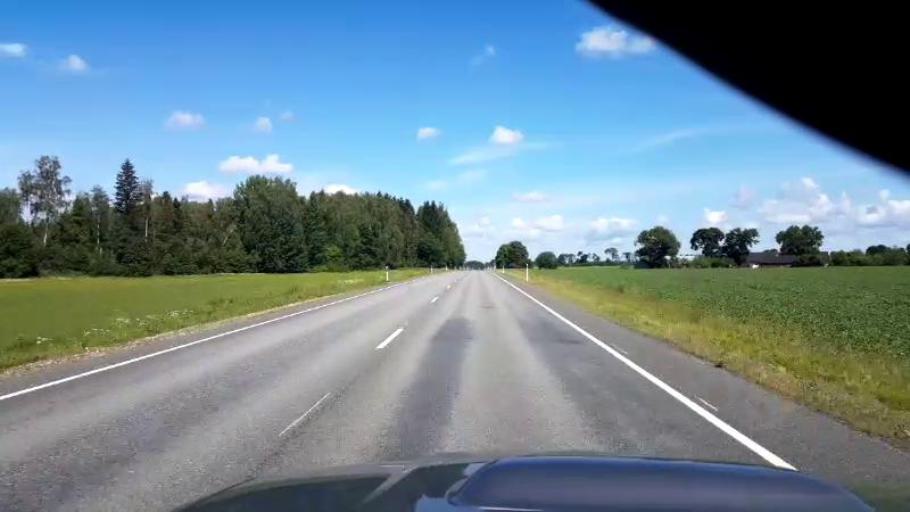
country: EE
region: Jaervamaa
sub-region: Jaerva-Jaani vald
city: Jarva-Jaani
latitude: 59.1627
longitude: 25.7613
